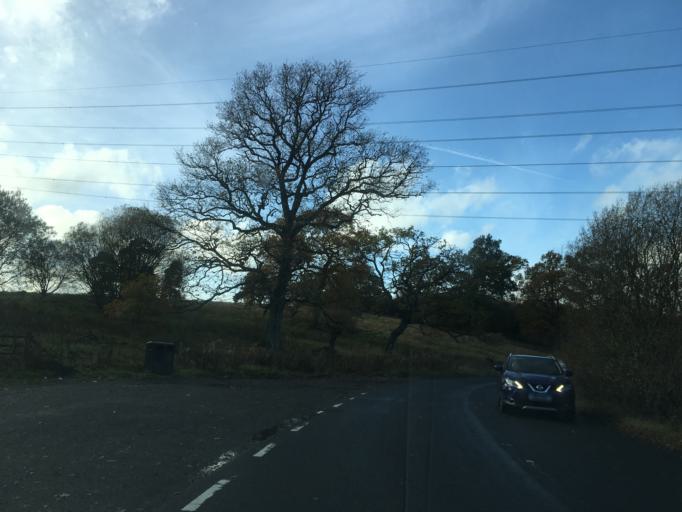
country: GB
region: Scotland
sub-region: Clackmannanshire
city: Dollar
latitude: 56.1460
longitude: -3.6487
